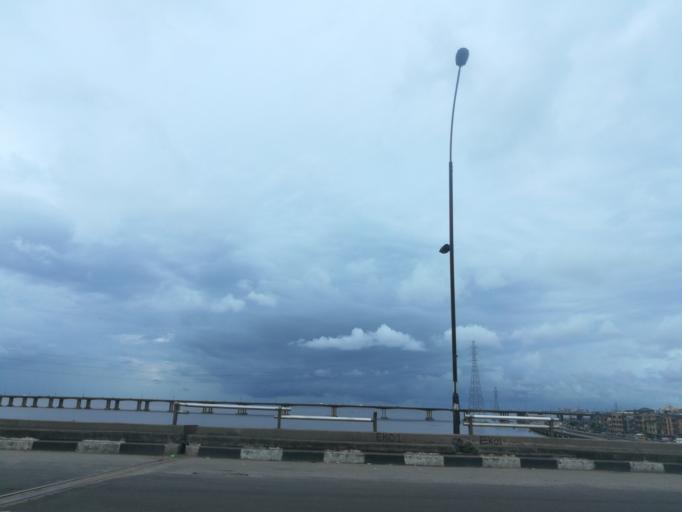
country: NG
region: Lagos
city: Lagos
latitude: 6.4656
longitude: 3.3856
